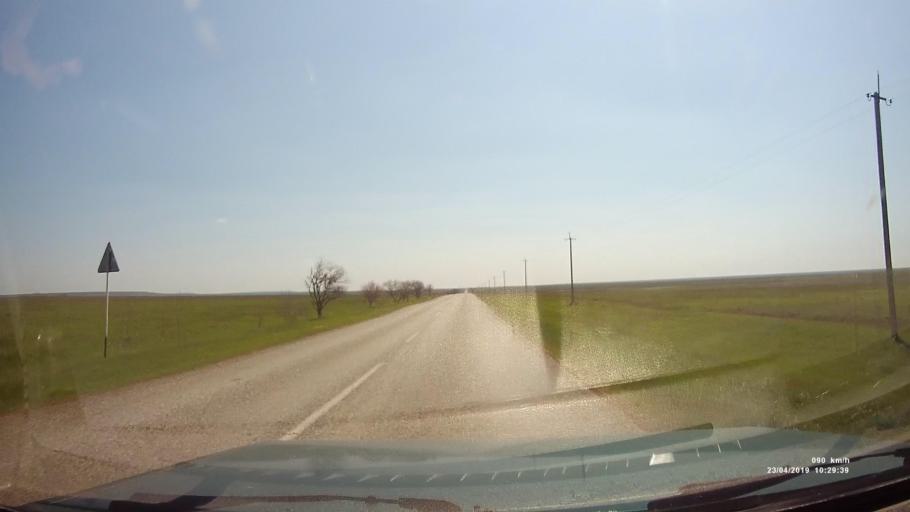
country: RU
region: Kalmykiya
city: Yashalta
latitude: 46.5971
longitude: 42.5303
